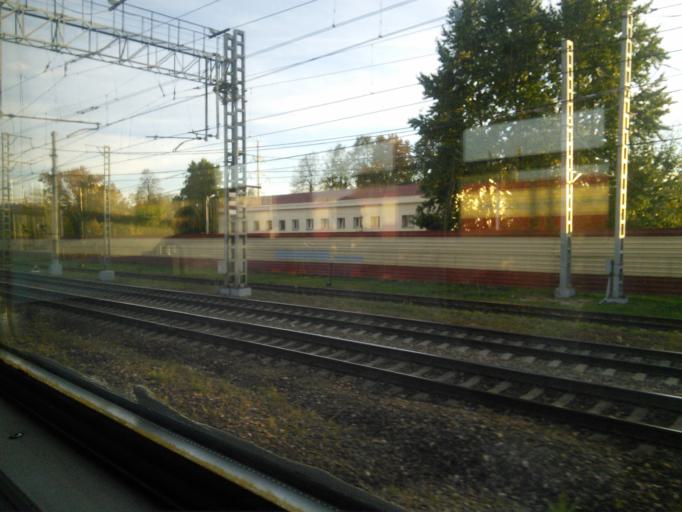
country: RU
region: Moscow
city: Ostankinskiy
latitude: 55.8151
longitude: 37.6070
